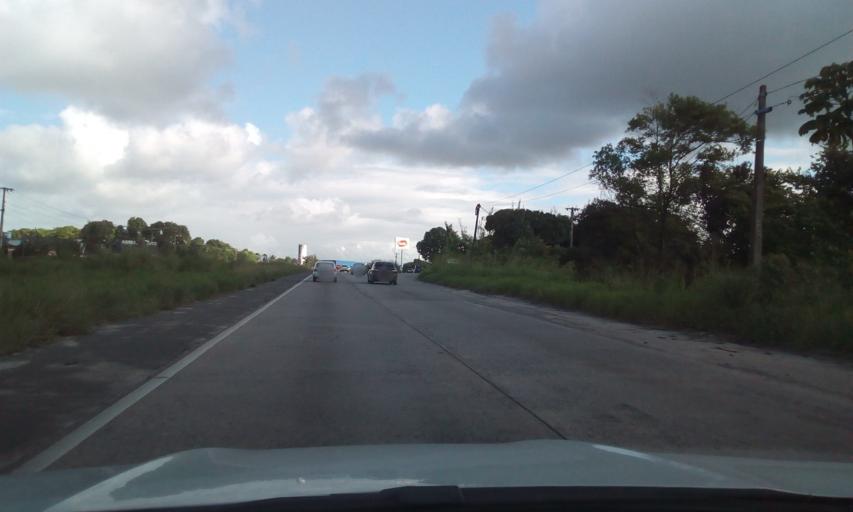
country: BR
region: Pernambuco
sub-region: Paulista
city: Paulista
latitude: -7.9568
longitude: -34.9120
